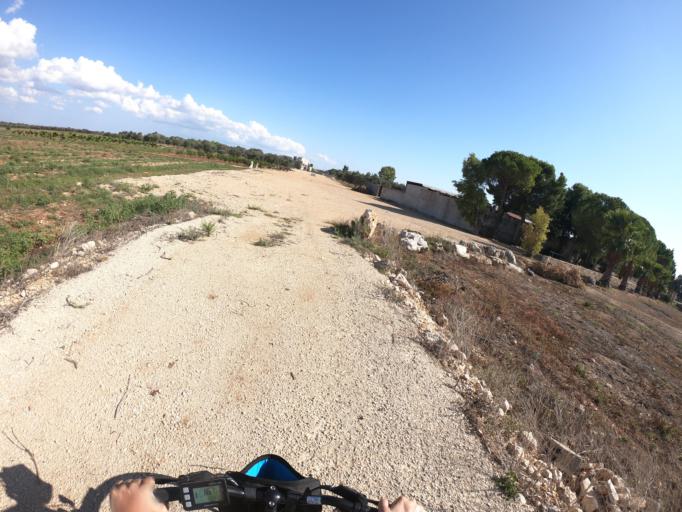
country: IT
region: Apulia
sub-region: Provincia di Lecce
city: Leverano
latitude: 40.2232
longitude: 17.9728
